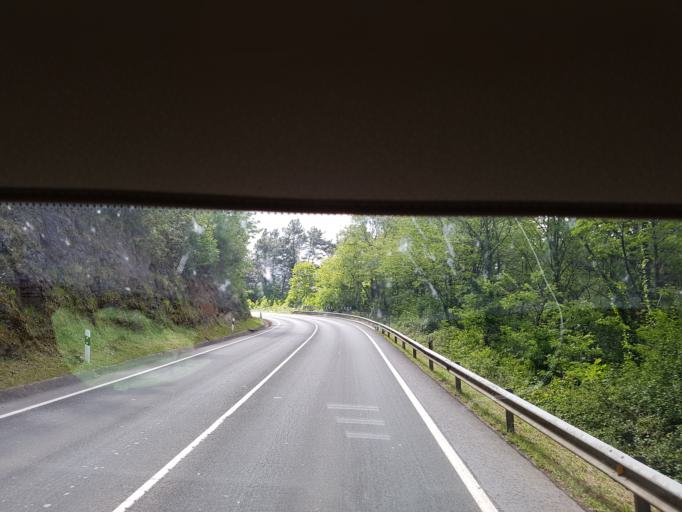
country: ES
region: Basque Country
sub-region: Bizkaia
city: Sopuerta
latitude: 43.2763
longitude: -3.1419
